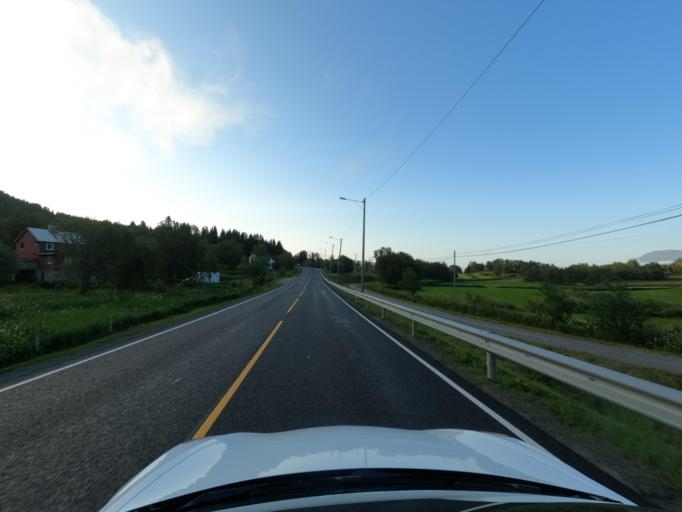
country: NO
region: Troms
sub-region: Skanland
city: Evenskjer
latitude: 68.6673
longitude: 16.5759
